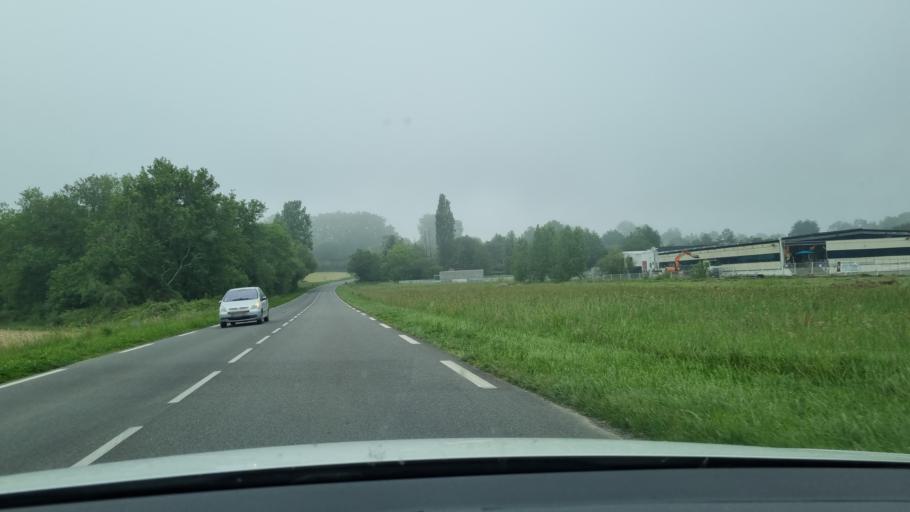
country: FR
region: Aquitaine
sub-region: Departement des Landes
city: Hagetmau
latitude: 43.6551
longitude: -0.6051
